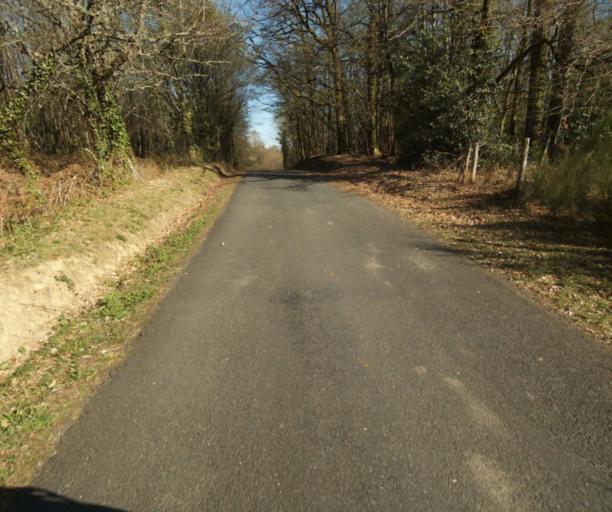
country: FR
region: Limousin
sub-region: Departement de la Correze
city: Saint-Mexant
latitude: 45.2898
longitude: 1.7037
